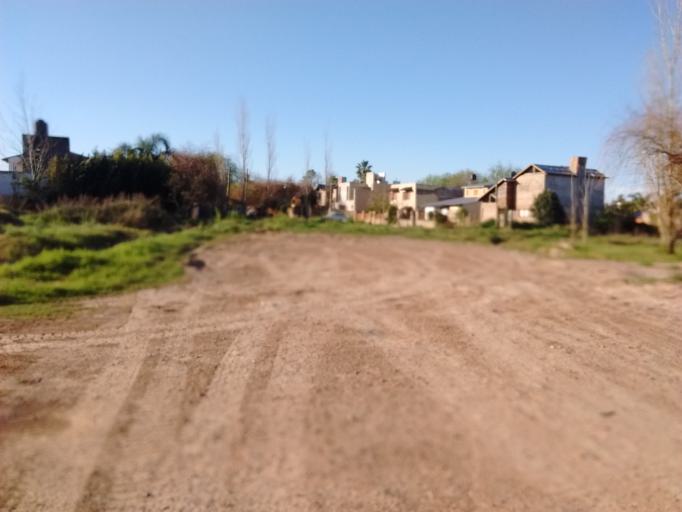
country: AR
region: Santa Fe
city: Funes
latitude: -32.9262
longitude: -60.7928
